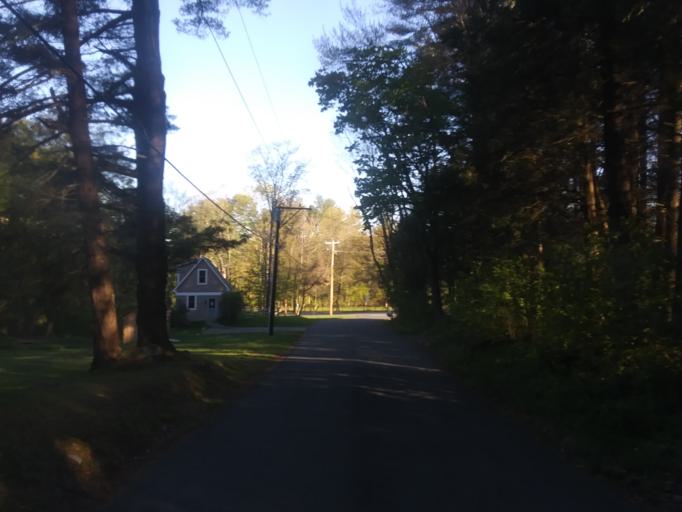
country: US
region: Massachusetts
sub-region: Franklin County
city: Shelburne Falls
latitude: 42.6131
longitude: -72.7657
